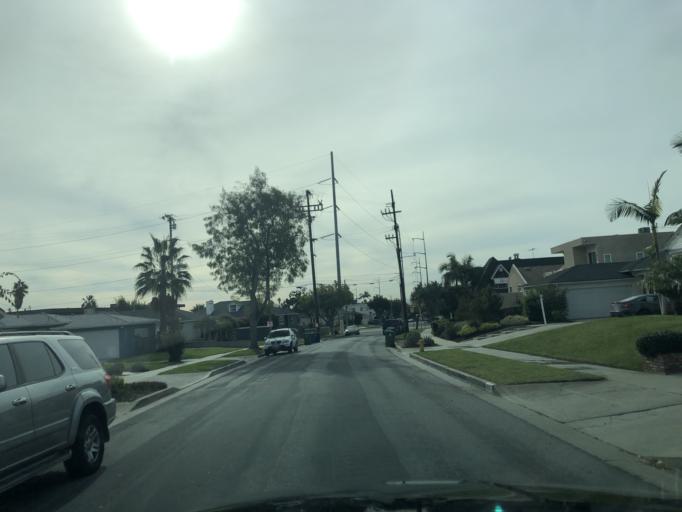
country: US
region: California
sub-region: Los Angeles County
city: View Park-Windsor Hills
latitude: 33.9823
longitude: -118.3601
